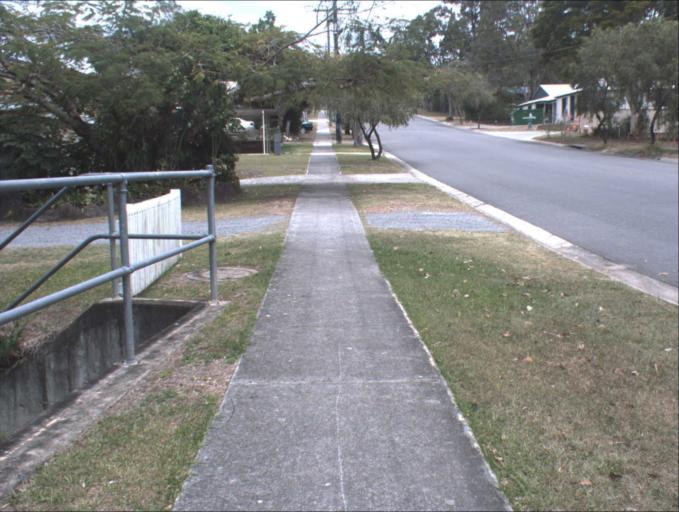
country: AU
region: Queensland
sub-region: Logan
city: Slacks Creek
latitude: -27.6479
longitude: 153.1658
